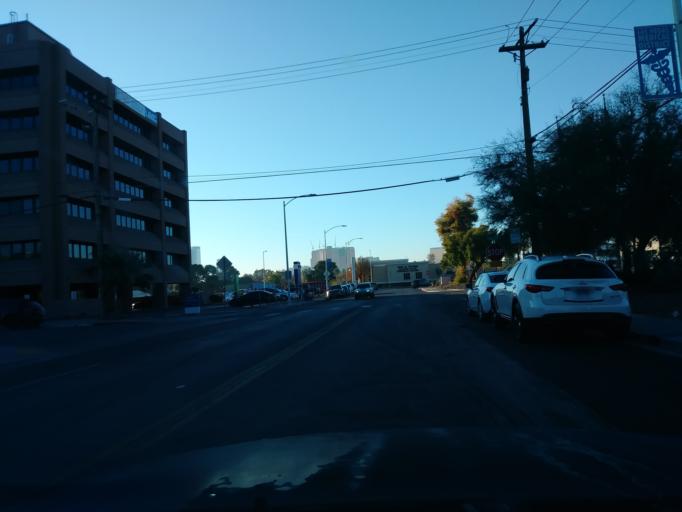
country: US
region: Nevada
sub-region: Clark County
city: Las Vegas
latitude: 36.1600
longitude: -115.1701
